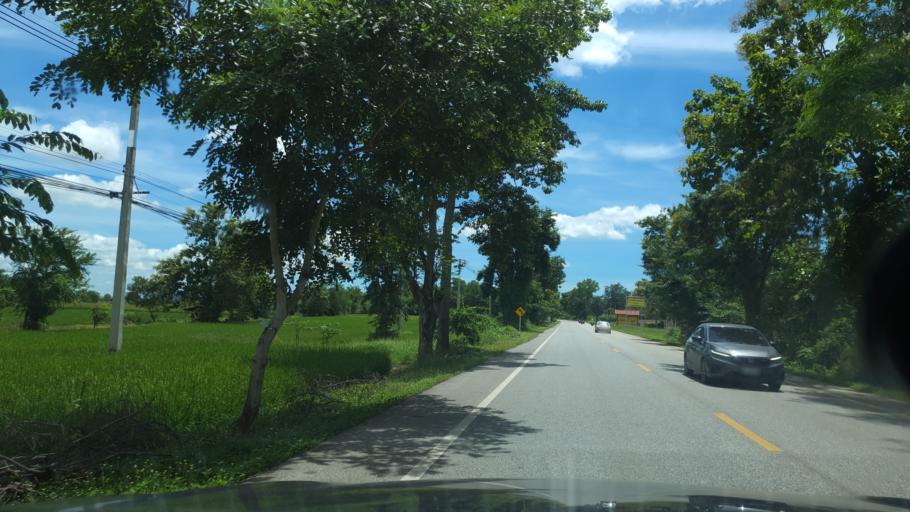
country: TH
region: Sukhothai
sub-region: Amphoe Si Satchanalai
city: Si Satchanalai
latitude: 17.4836
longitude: 99.7616
